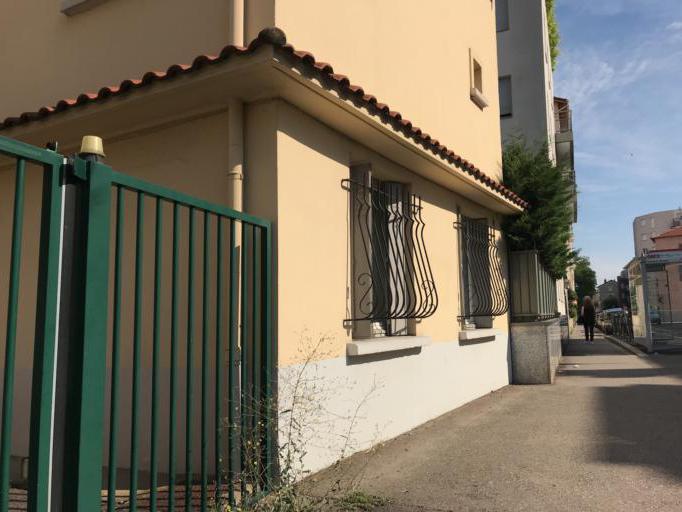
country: FR
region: Rhone-Alpes
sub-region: Departement du Rhone
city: Villeurbanne
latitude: 45.7497
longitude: 4.8734
